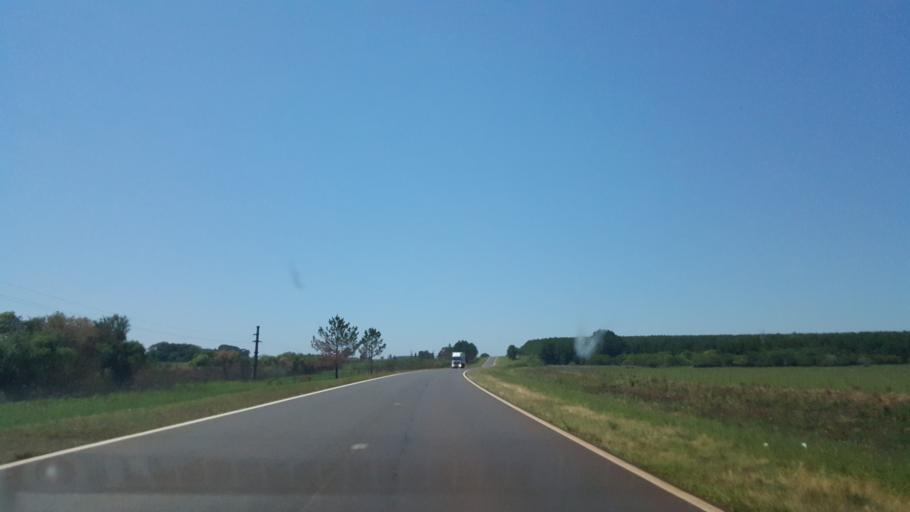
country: AR
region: Corrientes
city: Santo Tome
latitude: -28.3827
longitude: -56.1078
